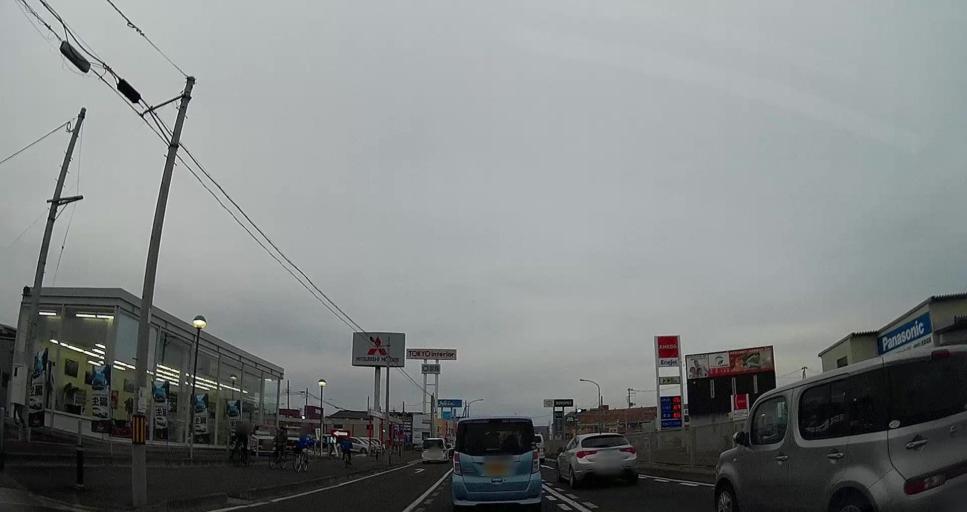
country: JP
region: Miyagi
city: Iwanuma
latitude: 38.1790
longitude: 140.8905
